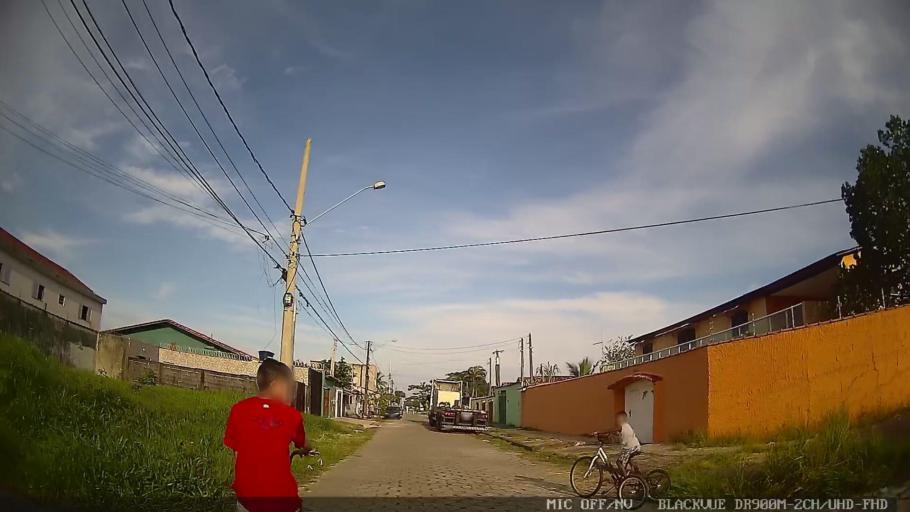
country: BR
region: Sao Paulo
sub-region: Itanhaem
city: Itanhaem
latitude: -24.1635
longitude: -46.7682
